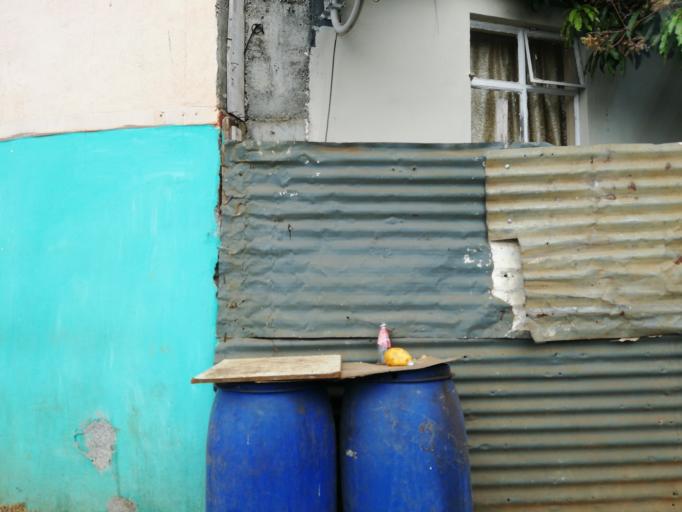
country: MU
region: Black River
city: Petite Riviere
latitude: -20.2212
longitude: 57.4593
